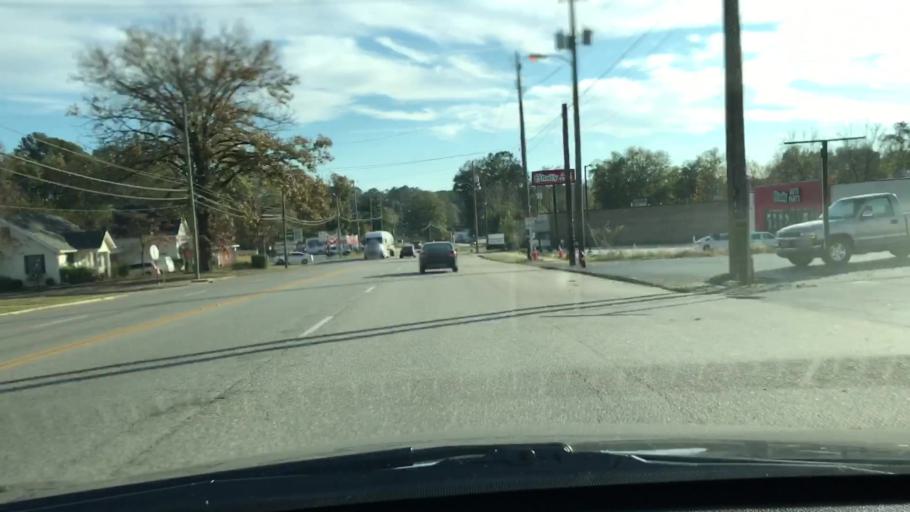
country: US
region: Alabama
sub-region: Cleburne County
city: Heflin
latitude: 33.6457
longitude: -85.5877
